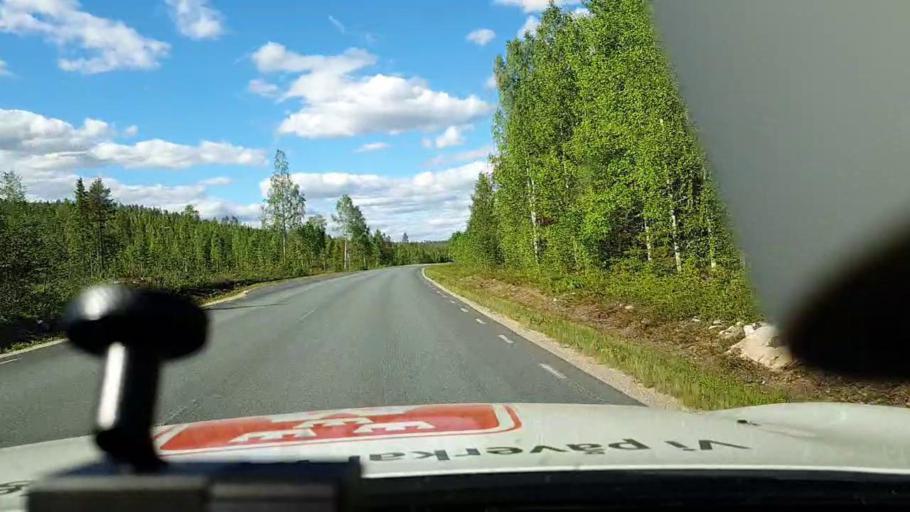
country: FI
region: Lapland
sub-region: Torniolaakso
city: Ylitornio
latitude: 66.3150
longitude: 23.6195
